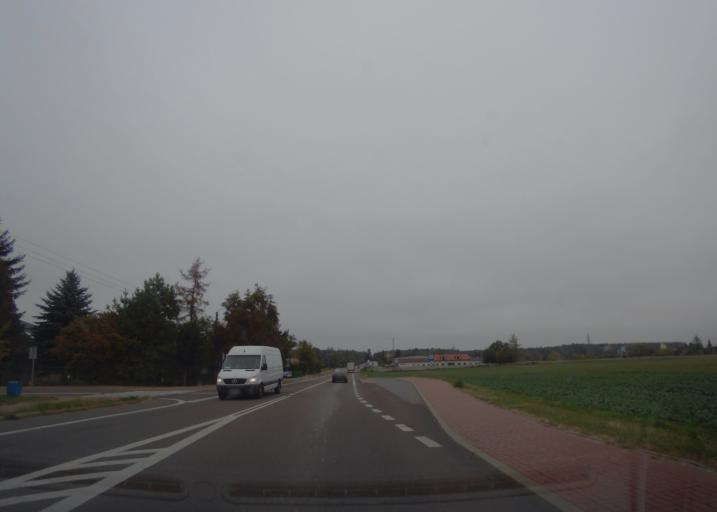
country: PL
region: Lublin Voivodeship
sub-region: Powiat krasnostawski
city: Krasnystaw
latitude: 50.9924
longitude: 23.1853
